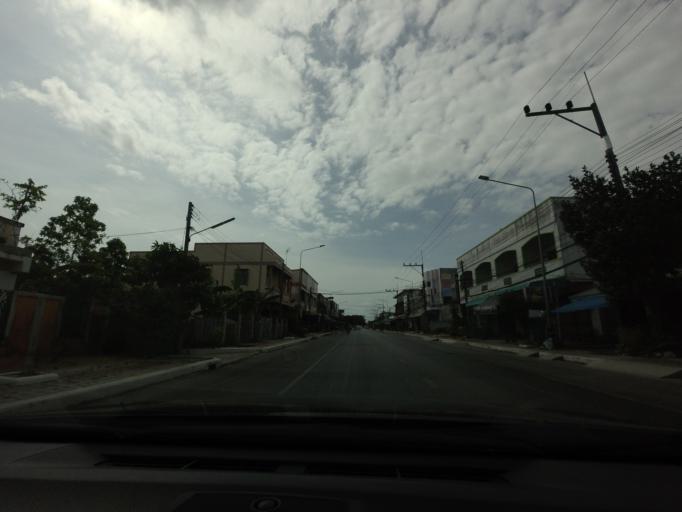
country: TH
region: Pattani
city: Pattani
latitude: 6.8793
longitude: 101.2472
